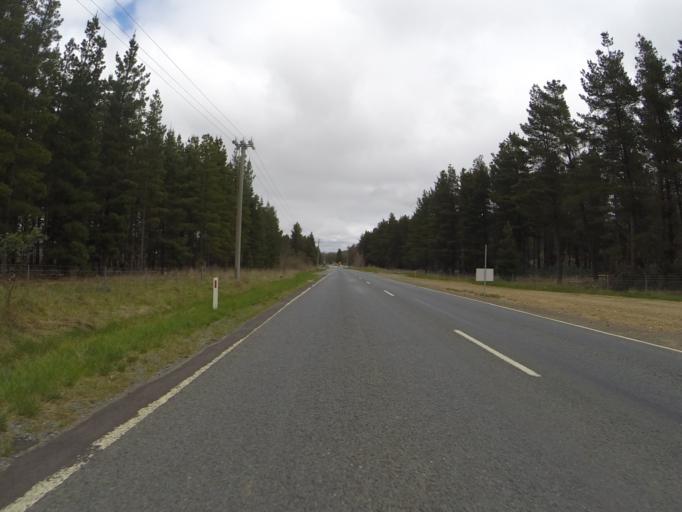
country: AU
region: Australian Capital Territory
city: Canberra
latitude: -35.2410
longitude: 149.1949
